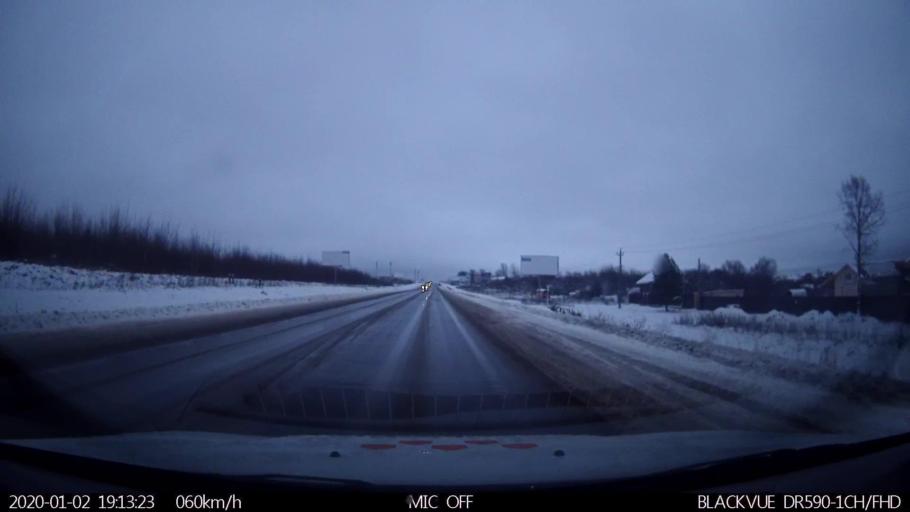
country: RU
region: Nizjnij Novgorod
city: Burevestnik
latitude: 56.2023
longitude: 43.8538
